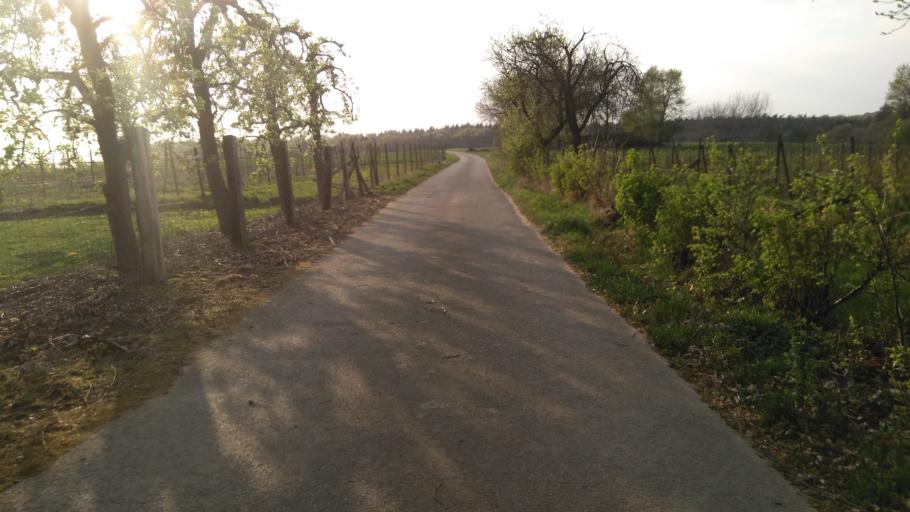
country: DE
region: Lower Saxony
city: Nottensdorf
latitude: 53.4701
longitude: 9.6317
